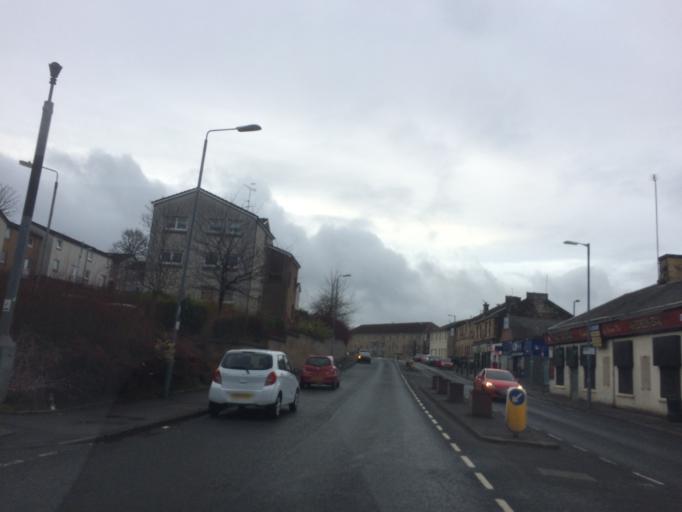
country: GB
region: Scotland
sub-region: East Renfrewshire
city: Giffnock
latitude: 55.8072
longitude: -4.3169
